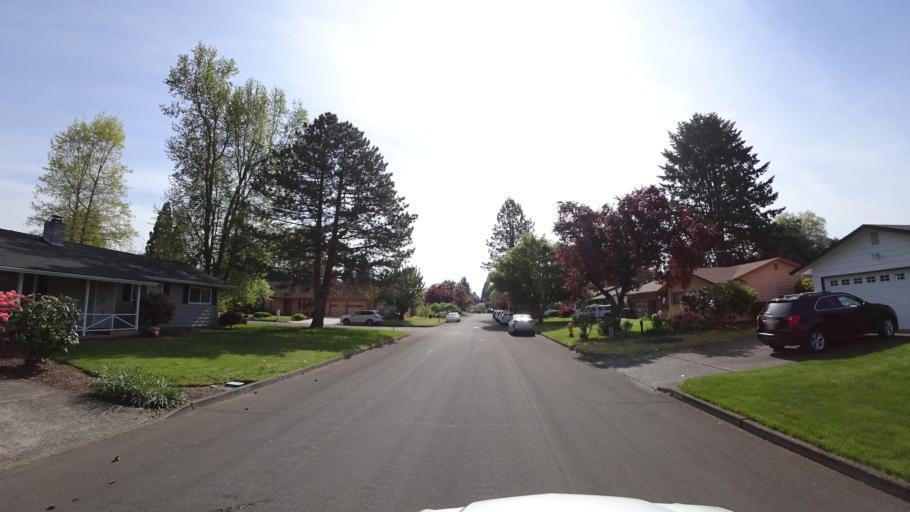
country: US
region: Oregon
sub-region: Washington County
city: Hillsboro
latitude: 45.5213
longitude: -122.9516
